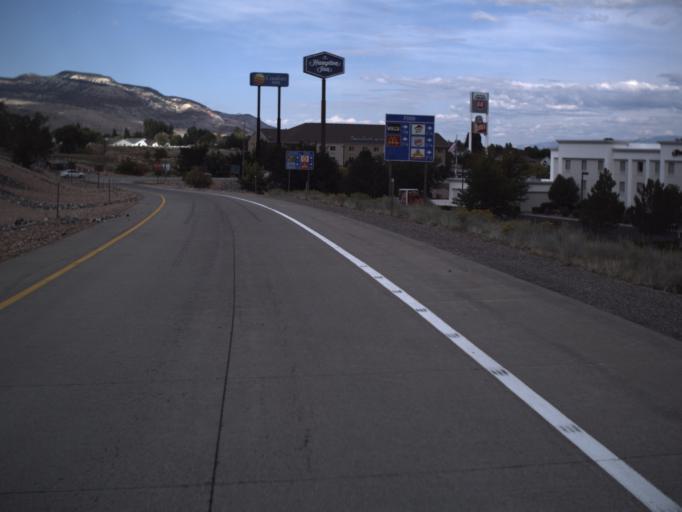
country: US
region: Utah
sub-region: Sevier County
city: Richfield
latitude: 38.7480
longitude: -112.1061
